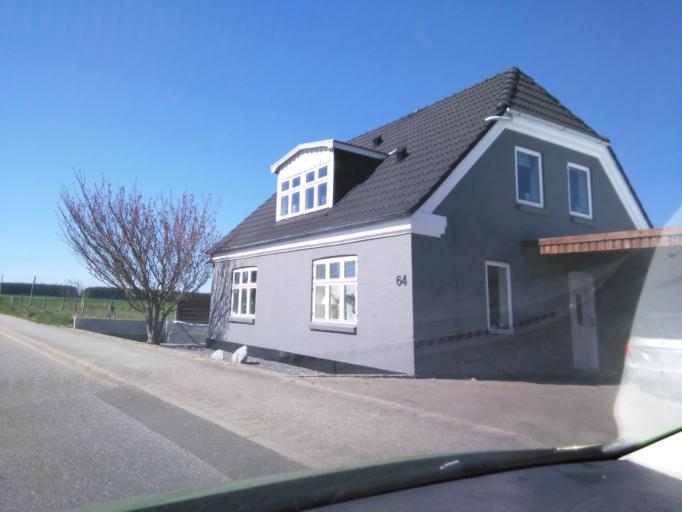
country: DK
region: South Denmark
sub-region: Varde Kommune
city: Oksbol
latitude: 55.6230
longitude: 8.3649
